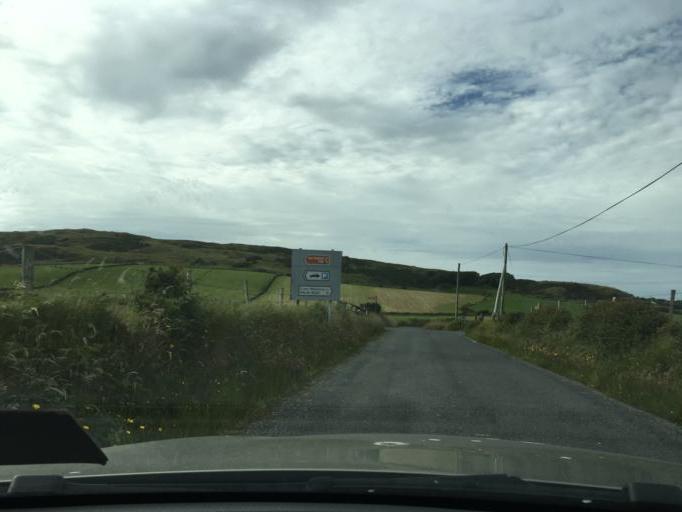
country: IE
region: Ulster
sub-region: County Donegal
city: Carndonagh
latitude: 55.3287
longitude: -7.3130
